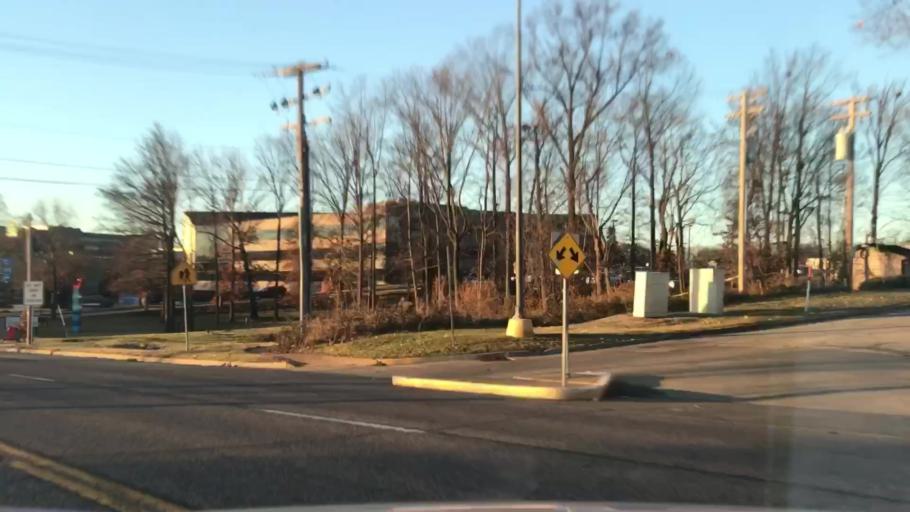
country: US
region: Missouri
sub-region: Saint Louis County
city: Kirkwood
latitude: 38.5620
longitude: -90.4069
